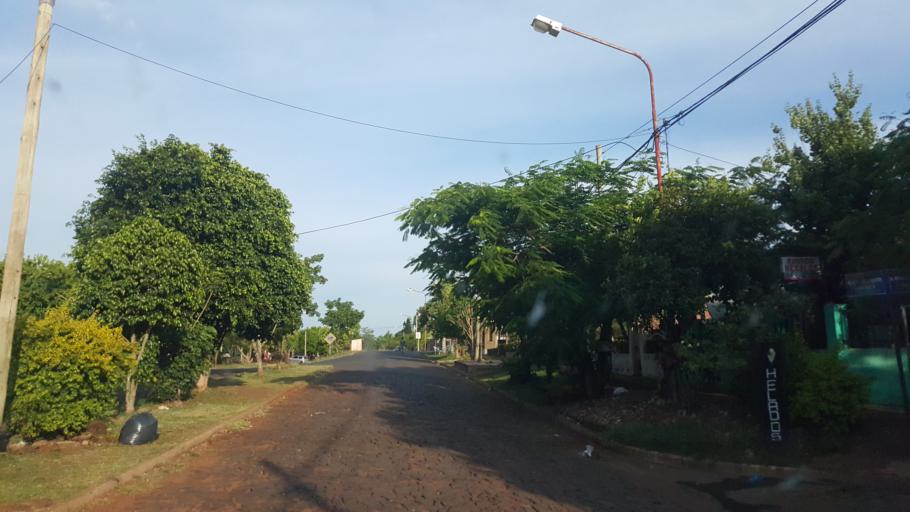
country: AR
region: Misiones
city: Garupa
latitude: -27.4361
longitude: -55.8707
